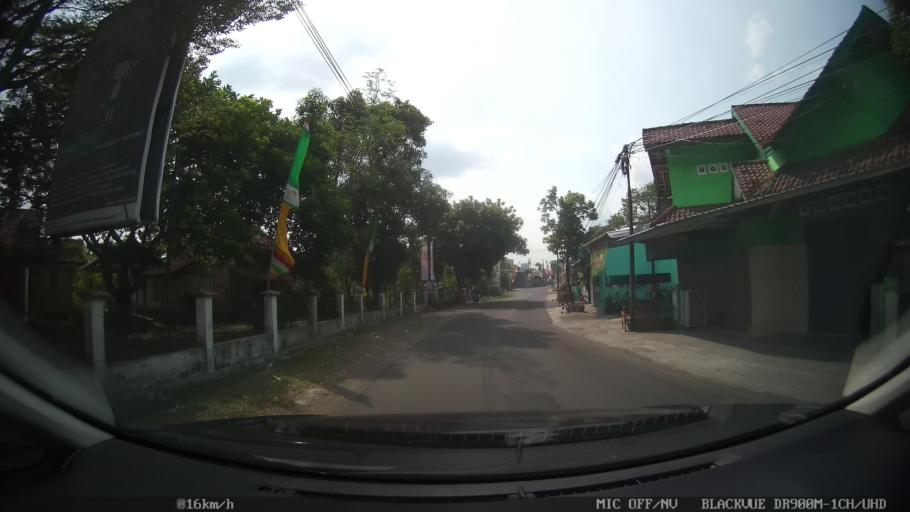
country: ID
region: Daerah Istimewa Yogyakarta
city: Depok
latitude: -7.7882
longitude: 110.4479
